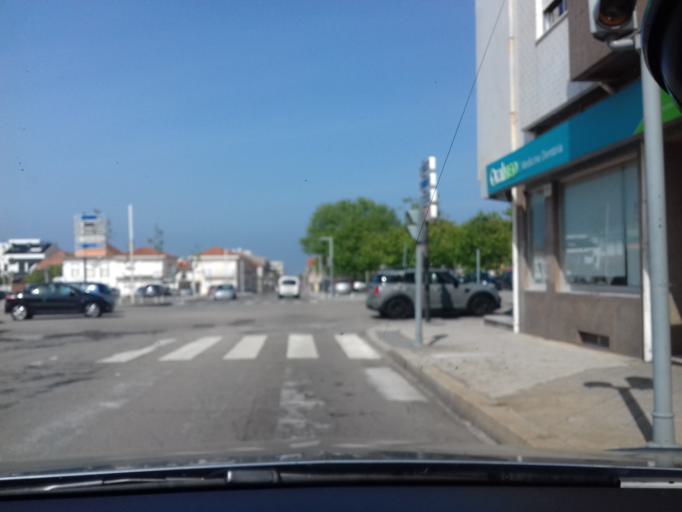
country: PT
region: Aveiro
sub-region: Espinho
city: Espinho
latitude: 41.0040
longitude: -8.6378
